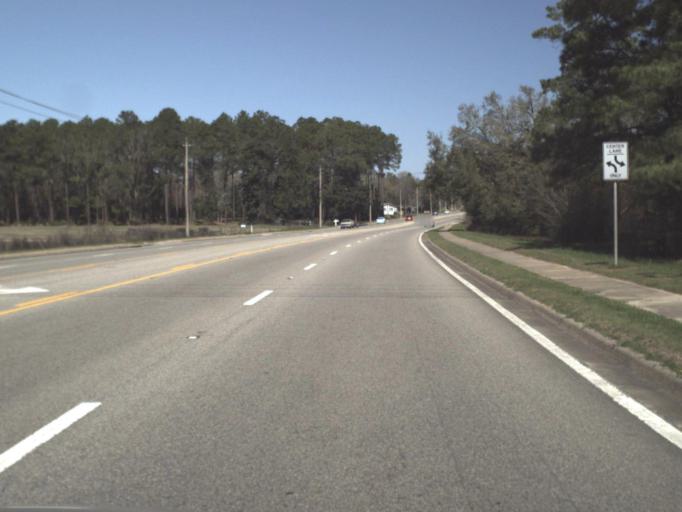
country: US
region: Florida
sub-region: Gadsden County
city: Quincy
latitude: 30.5670
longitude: -84.5930
